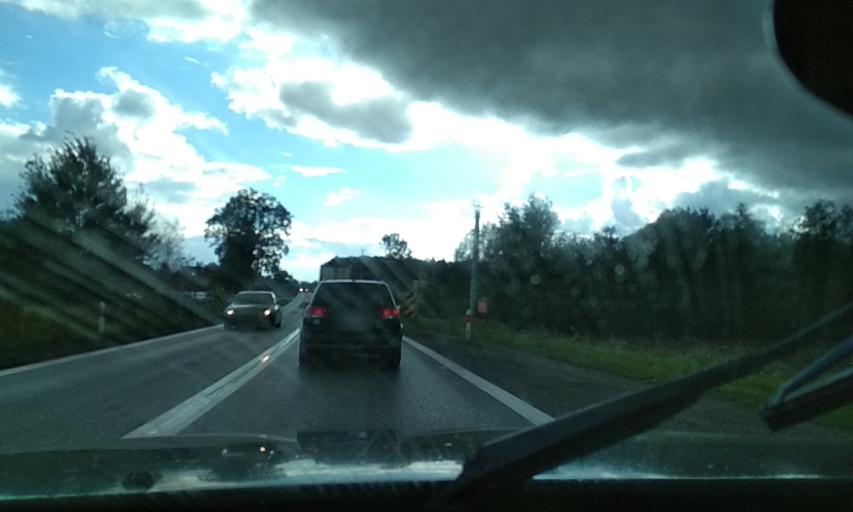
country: PL
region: Silesian Voivodeship
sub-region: Powiat gliwicki
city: Zernica
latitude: 50.2231
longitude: 18.6099
